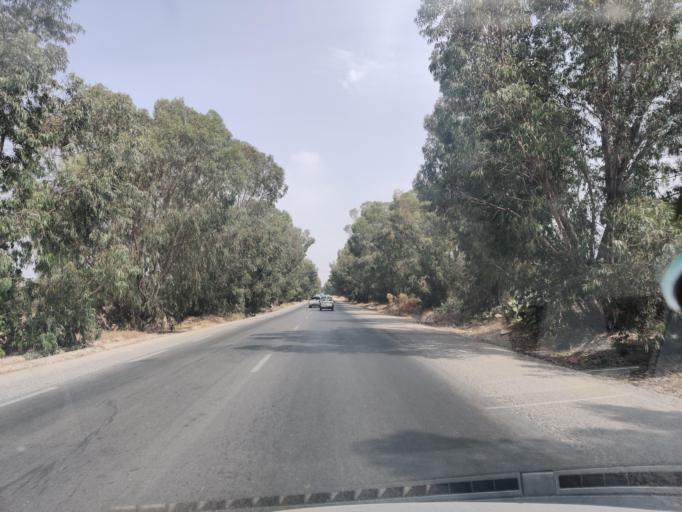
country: TN
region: Nabul
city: Al Hammamat
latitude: 36.4441
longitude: 10.5728
